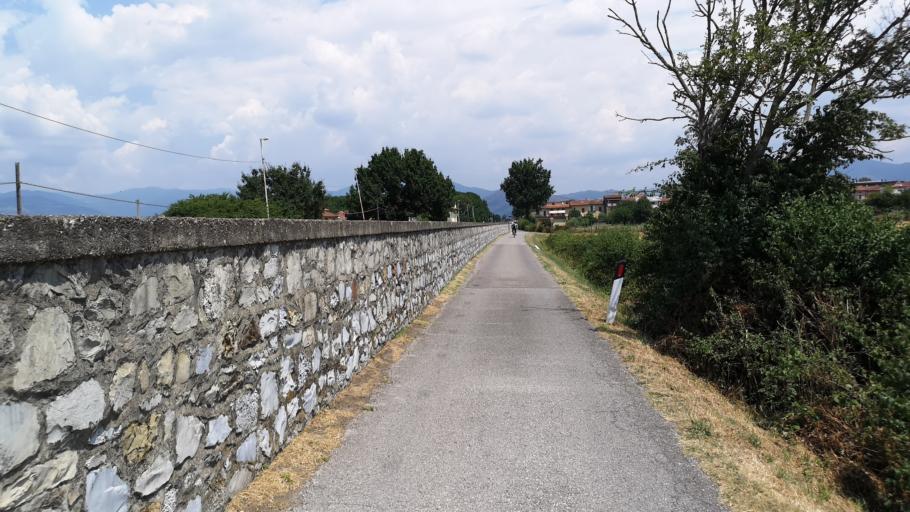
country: IT
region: Tuscany
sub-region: Provincia di Pistoia
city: Catena
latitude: 43.8618
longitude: 11.0356
